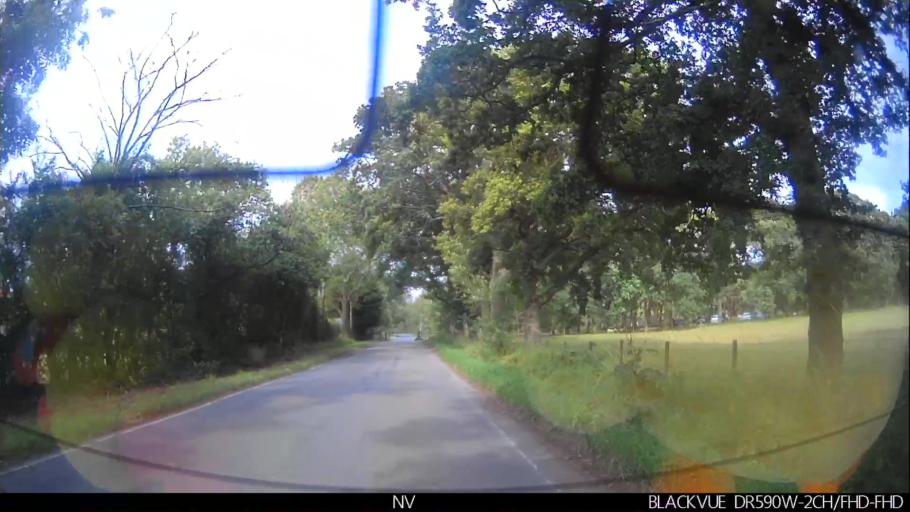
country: GB
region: England
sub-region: North Yorkshire
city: Strensall
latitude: 54.0422
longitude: -1.0125
